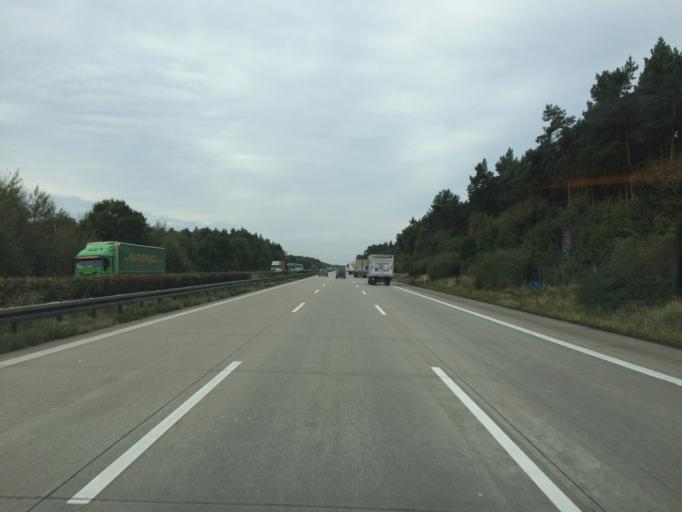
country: DE
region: Brandenburg
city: Wollin
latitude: 52.3332
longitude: 12.5038
